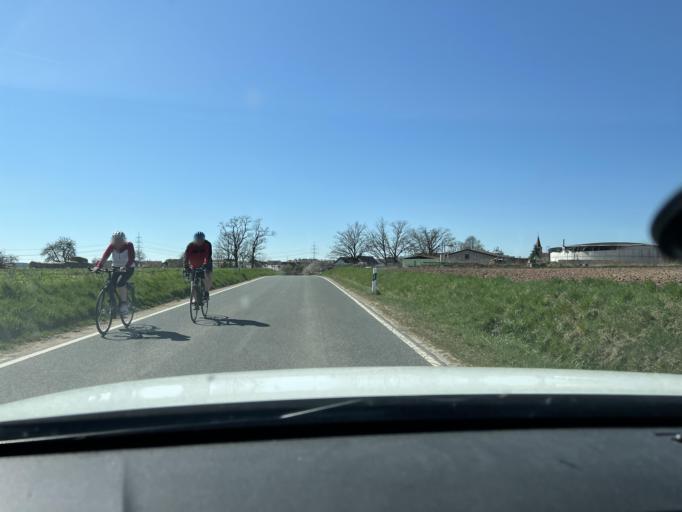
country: DE
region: Bavaria
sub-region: Regierungsbezirk Mittelfranken
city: Grosshabersdorf
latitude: 49.4325
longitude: 10.7636
